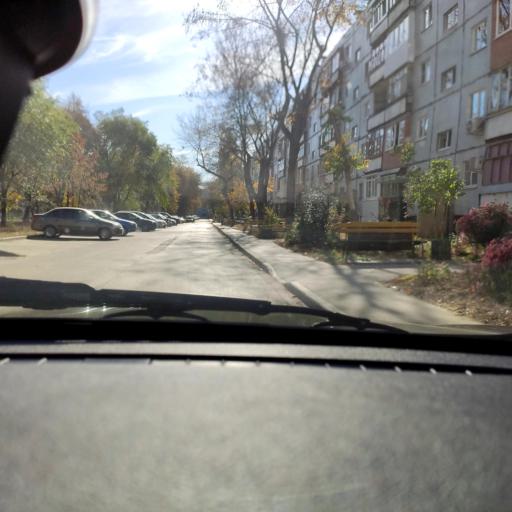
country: RU
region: Samara
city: Tol'yatti
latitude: 53.5242
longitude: 49.2718
